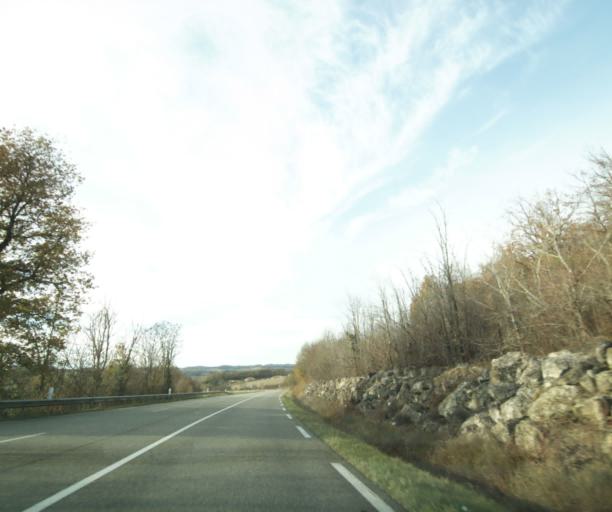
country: FR
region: Midi-Pyrenees
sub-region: Departement du Gers
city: Jegun
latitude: 43.7220
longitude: 0.3995
